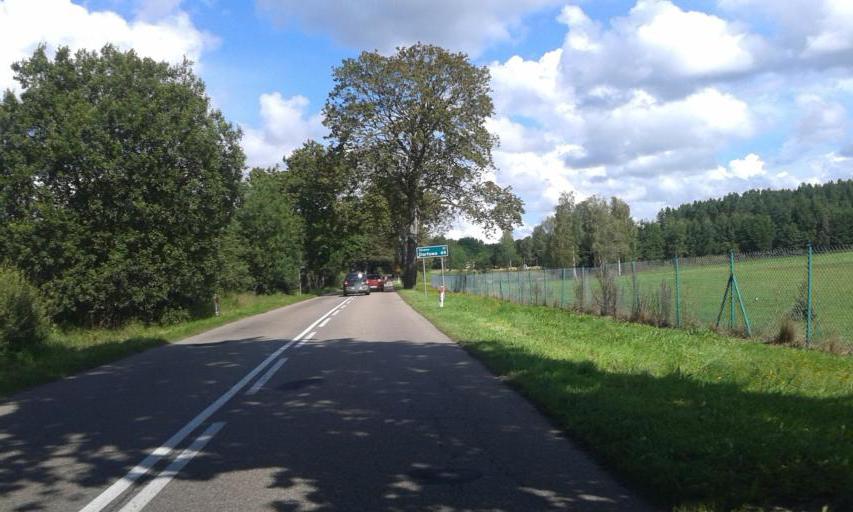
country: PL
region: West Pomeranian Voivodeship
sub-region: Powiat koszalinski
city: Polanow
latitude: 54.1993
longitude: 16.6980
